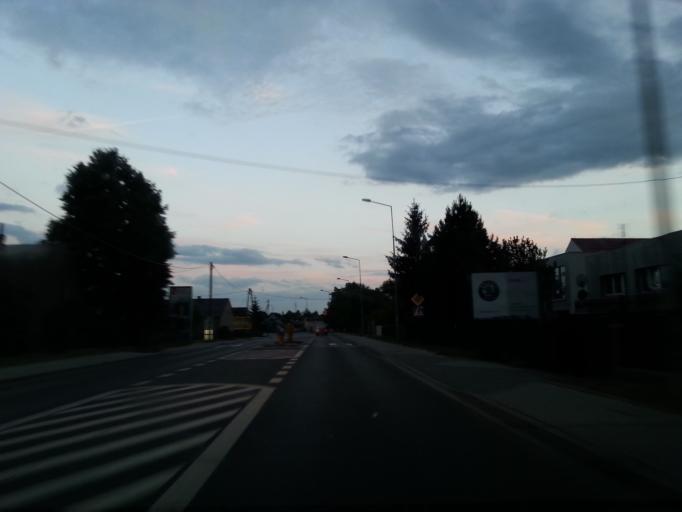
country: PL
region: Lower Silesian Voivodeship
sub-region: Powiat wroclawski
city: Bielany Wroclawskie
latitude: 51.0361
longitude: 16.9679
